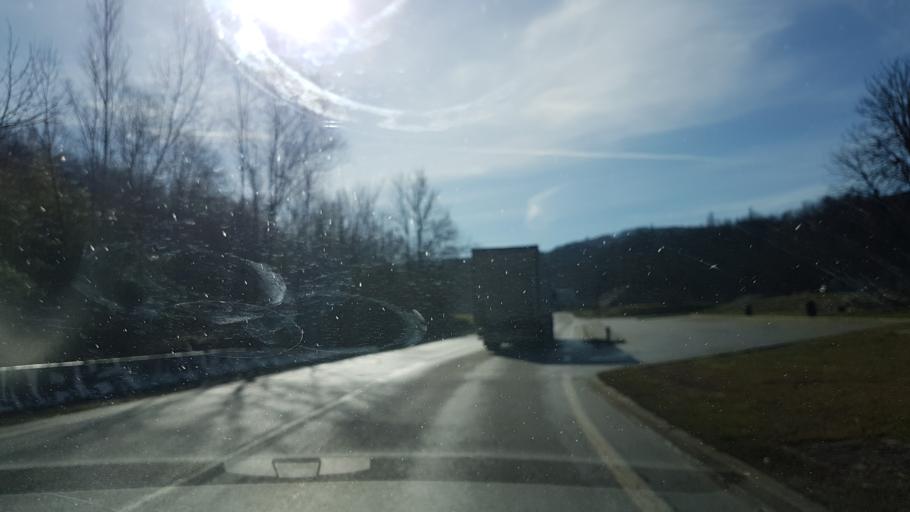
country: FR
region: Rhone-Alpes
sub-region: Departement de la Haute-Savoie
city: Frangy
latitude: 46.0231
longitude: 5.9097
